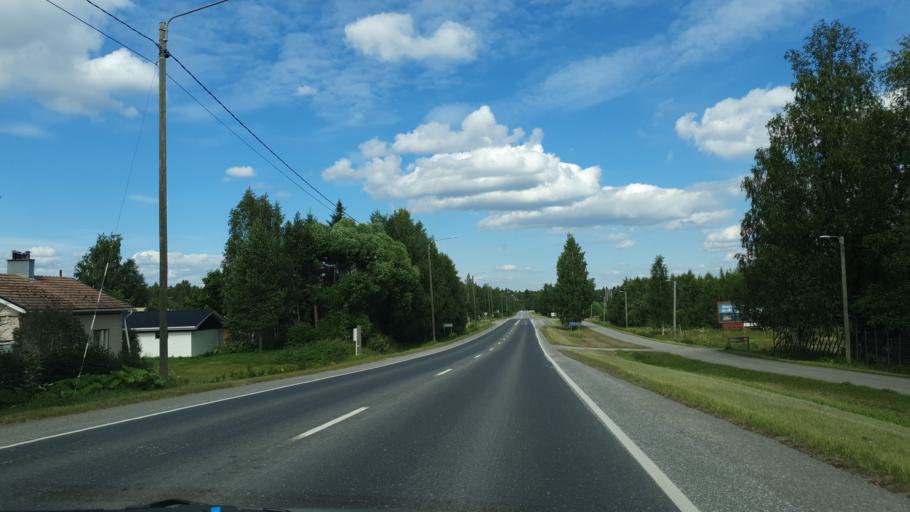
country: FI
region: Kainuu
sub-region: Kajaani
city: Kajaani
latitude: 64.2430
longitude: 27.7581
